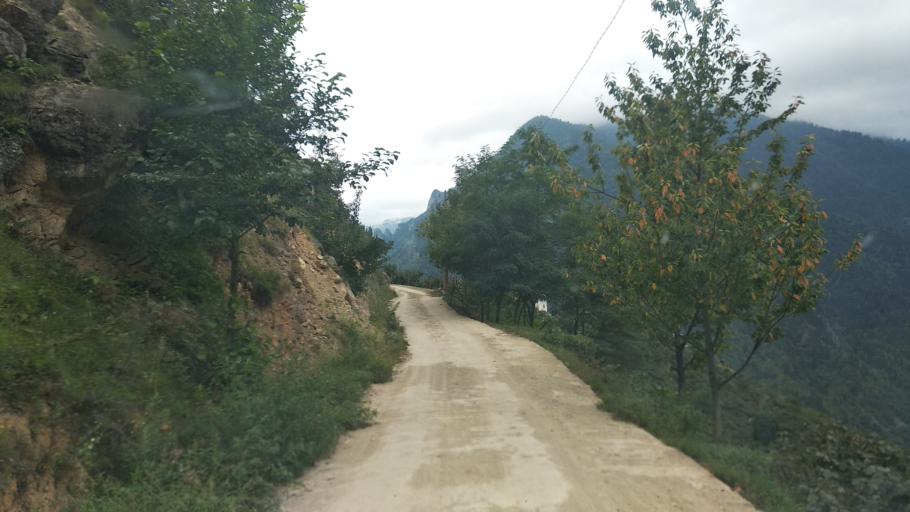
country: TR
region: Giresun
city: Dogankent
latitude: 40.7436
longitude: 38.9951
